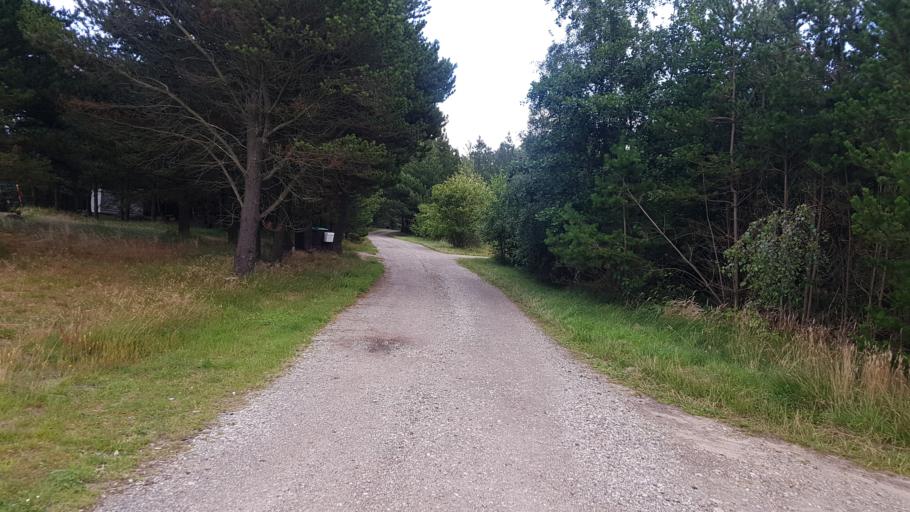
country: DE
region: Schleswig-Holstein
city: List
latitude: 55.0893
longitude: 8.5262
